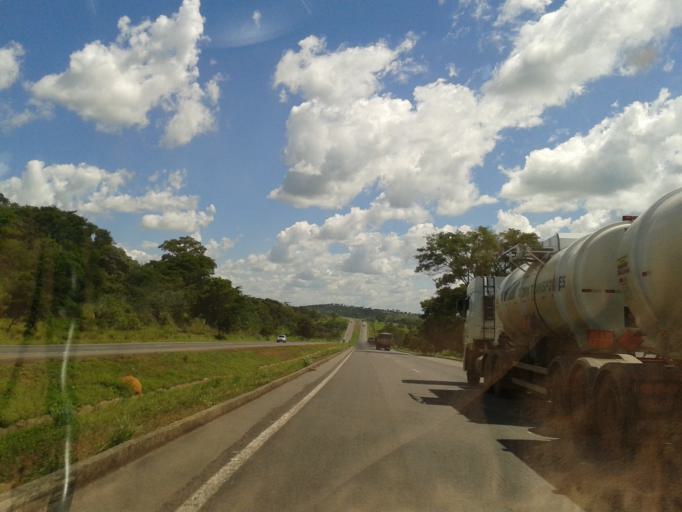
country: BR
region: Goias
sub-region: Piracanjuba
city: Piracanjuba
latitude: -17.3482
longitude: -49.2485
